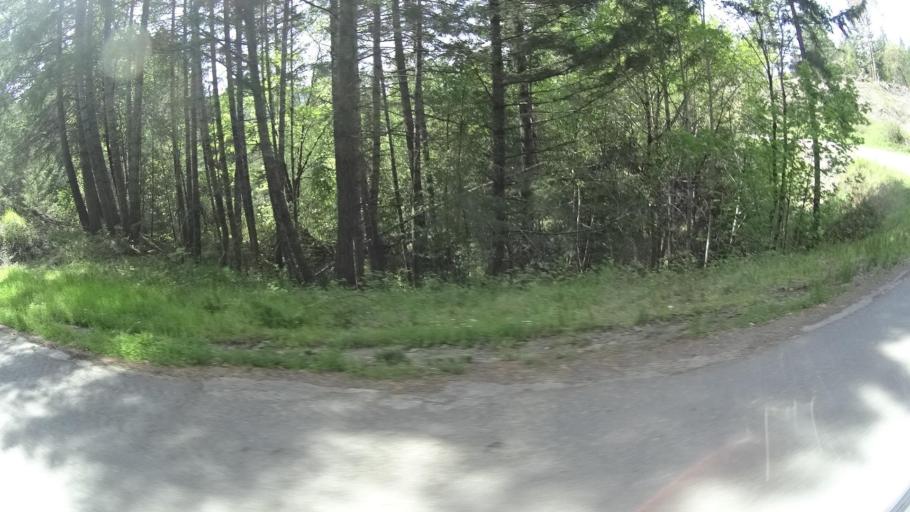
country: US
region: California
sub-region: Humboldt County
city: Redway
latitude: 40.3789
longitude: -123.7424
